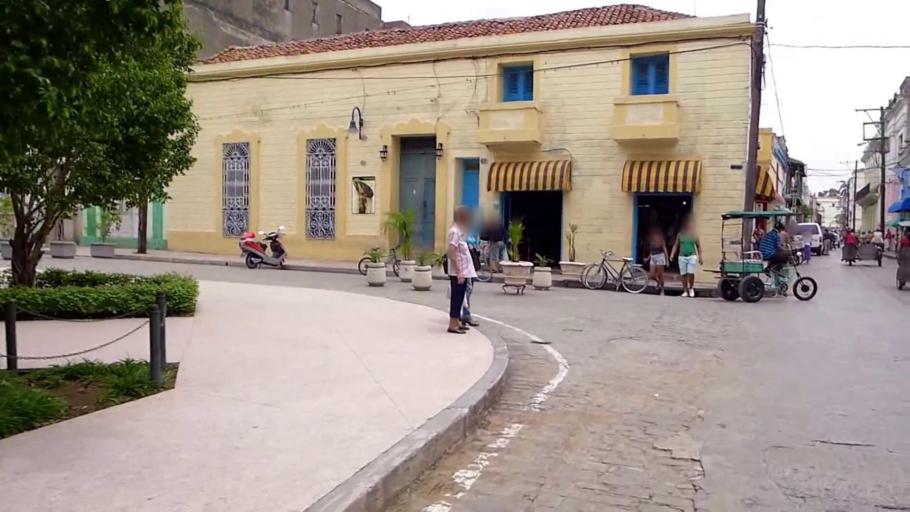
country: CU
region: Camaguey
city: Camaguey
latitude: 21.3794
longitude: -77.9182
